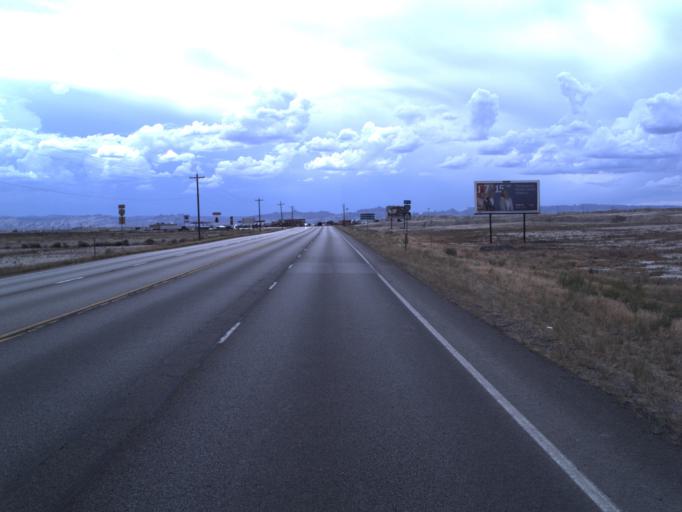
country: US
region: Utah
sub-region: Carbon County
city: East Carbon City
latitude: 38.9955
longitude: -110.1752
